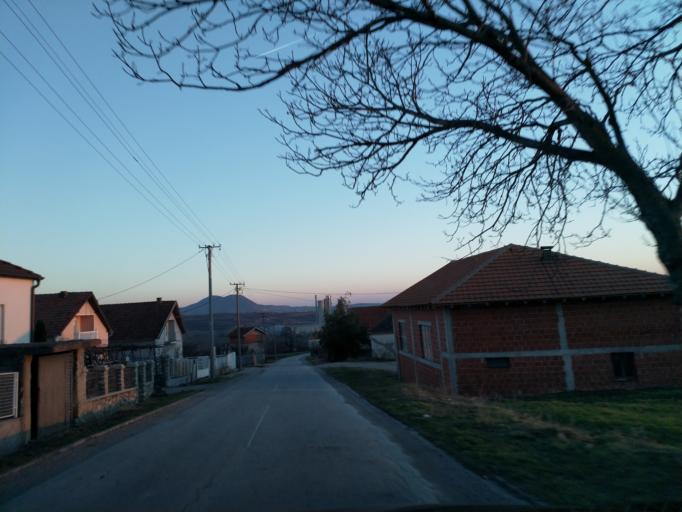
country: RS
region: Central Serbia
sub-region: Pomoravski Okrug
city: Paracin
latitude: 43.9215
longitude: 21.5105
